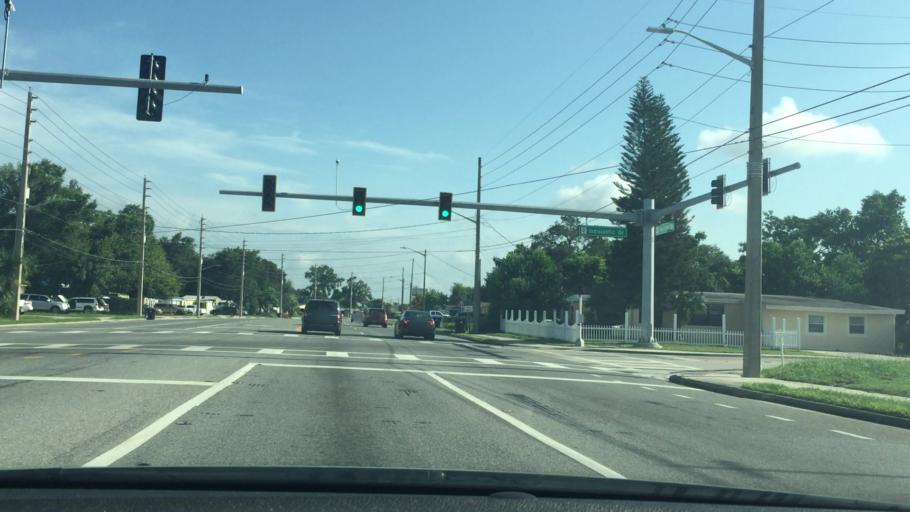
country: US
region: Florida
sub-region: Orange County
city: Pine Hills
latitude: 28.5726
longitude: -81.4518
